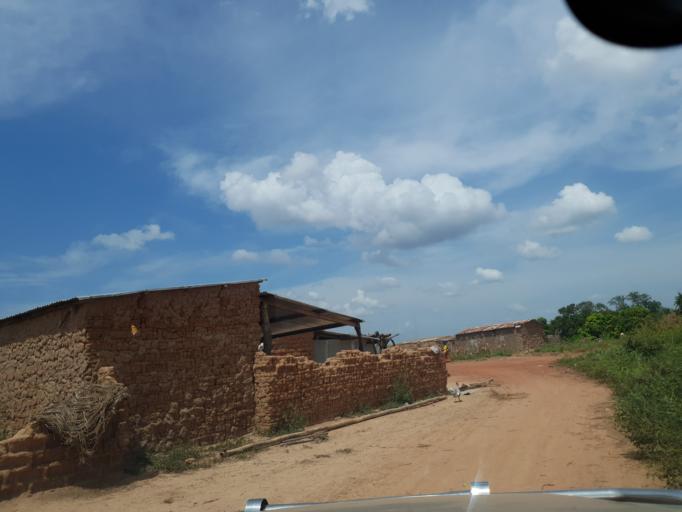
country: ML
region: Sikasso
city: Sikasso
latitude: 11.6736
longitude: -6.1627
